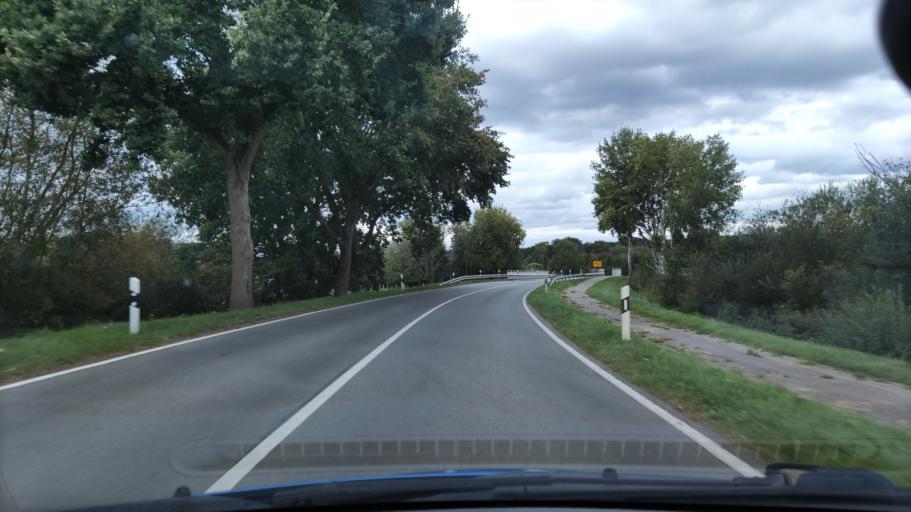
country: DE
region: Lower Saxony
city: Neu Darchau
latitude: 53.3004
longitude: 10.9683
